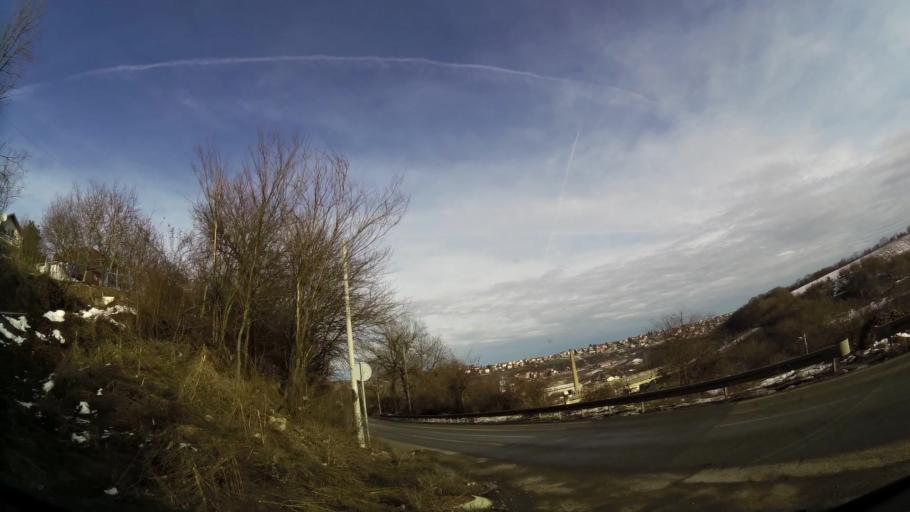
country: RS
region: Central Serbia
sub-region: Belgrade
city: Rakovica
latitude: 44.7210
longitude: 20.4331
